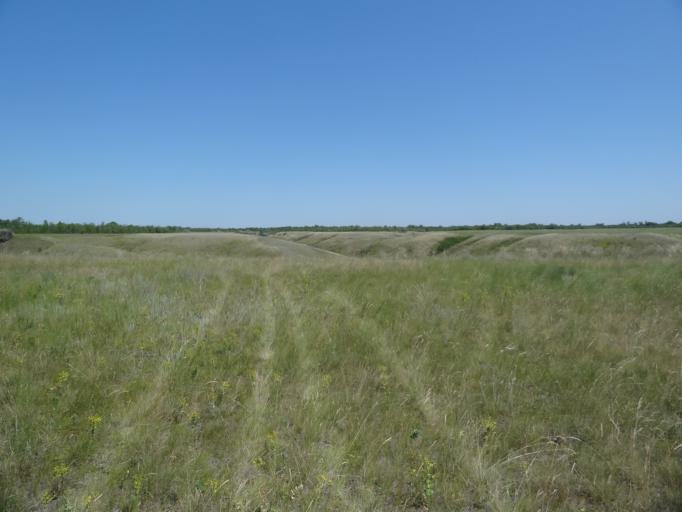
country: RU
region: Saratov
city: Krasnoarmeysk
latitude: 51.1475
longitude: 45.9353
